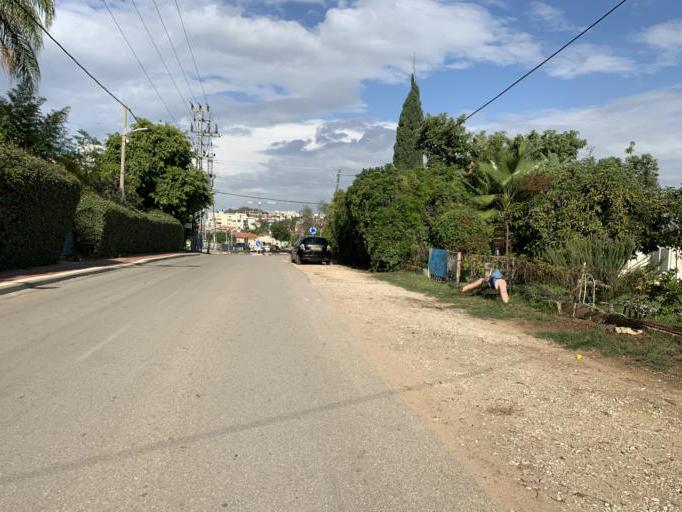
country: IL
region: Central District
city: Ra'anana
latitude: 32.1712
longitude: 34.8756
